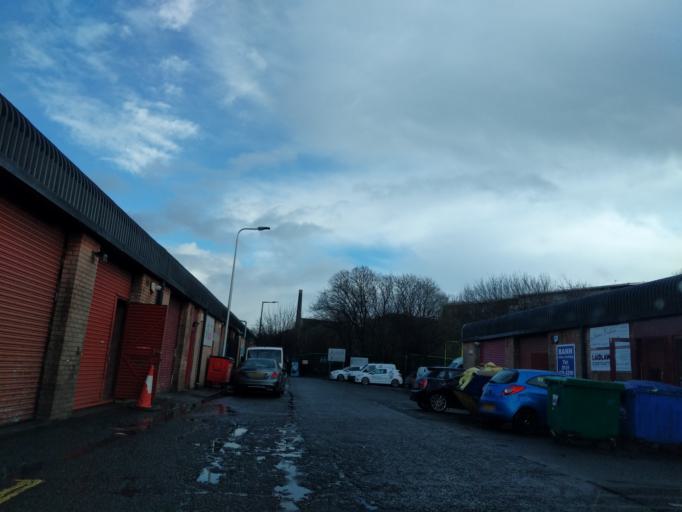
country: GB
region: Scotland
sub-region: Edinburgh
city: Edinburgh
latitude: 55.9431
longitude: -3.2273
